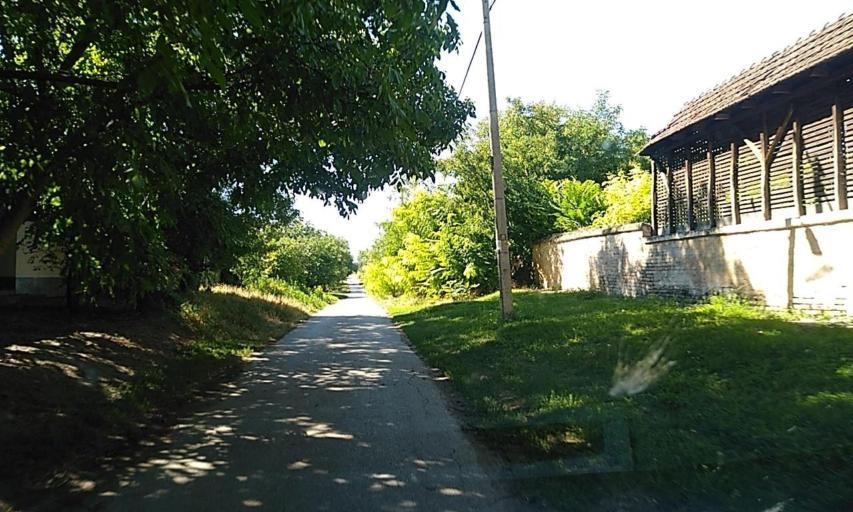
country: RS
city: Backo Gradiste
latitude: 45.5383
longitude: 20.0361
